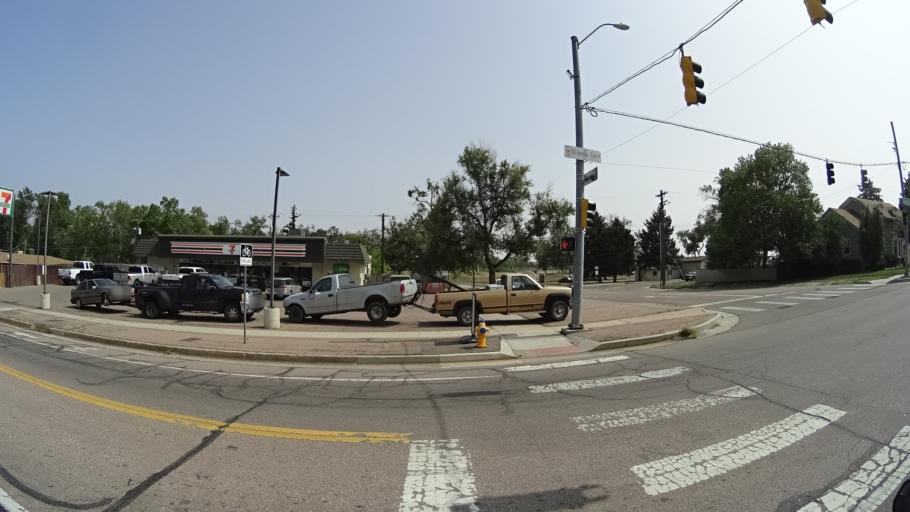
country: US
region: Colorado
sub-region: El Paso County
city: Colorado Springs
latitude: 38.8278
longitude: -104.8042
